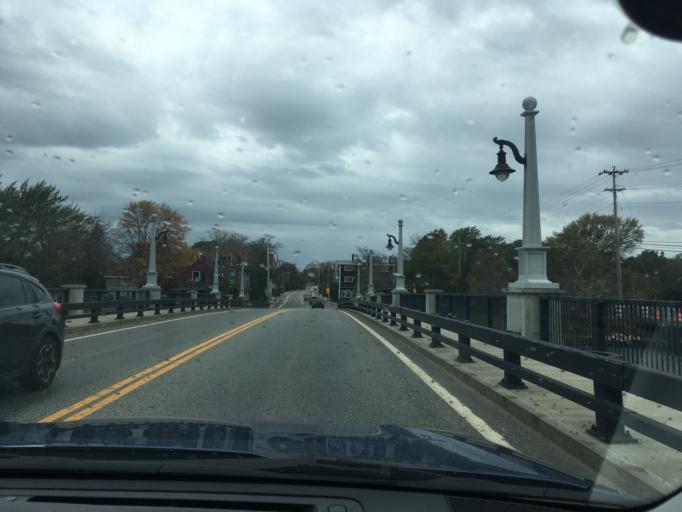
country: US
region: Rhode Island
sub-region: Bristol County
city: Warren
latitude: 41.7375
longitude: -71.2889
